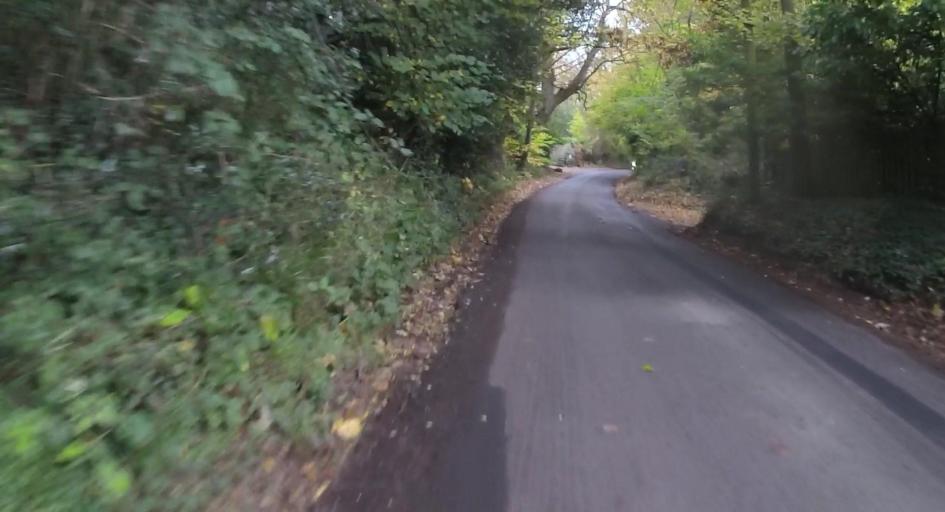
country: GB
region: England
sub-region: Wokingham
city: Finchampstead
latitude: 51.3666
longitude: -0.8593
